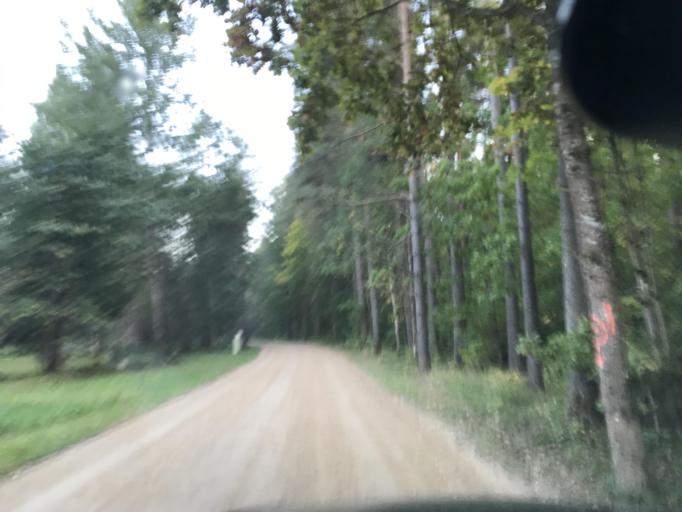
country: LV
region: Ikskile
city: Ikskile
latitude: 56.8291
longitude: 24.5121
